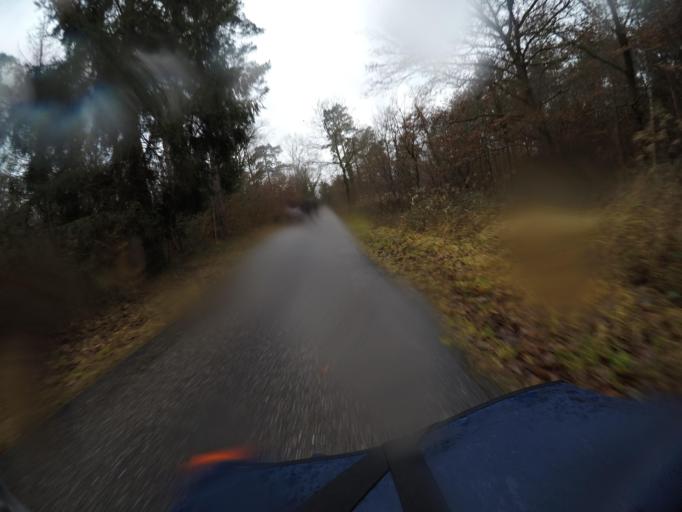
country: DE
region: Baden-Wuerttemberg
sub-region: Karlsruhe Region
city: Eggenstein-Leopoldshafen
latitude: 49.0548
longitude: 8.4351
